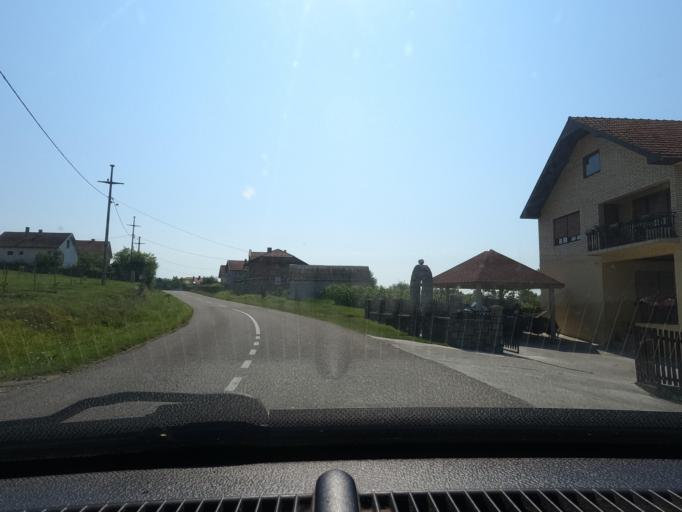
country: RS
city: Jadranska Lesnica
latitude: 44.5527
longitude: 19.3255
